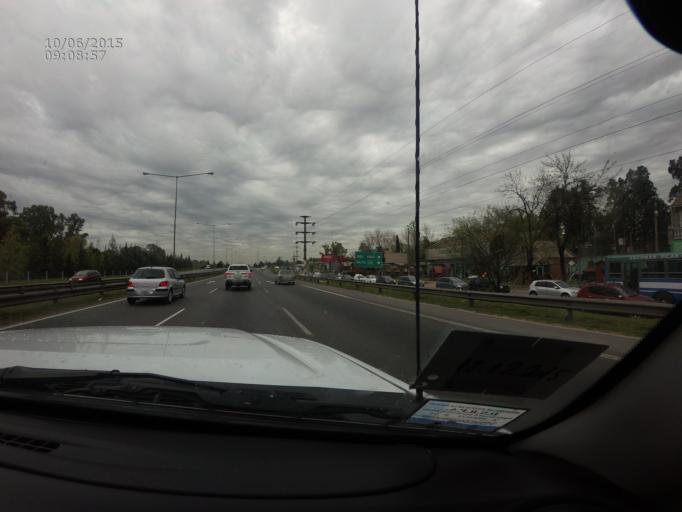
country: AR
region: Buenos Aires
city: Santa Catalina - Dique Lujan
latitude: -34.3833
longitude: -58.7491
